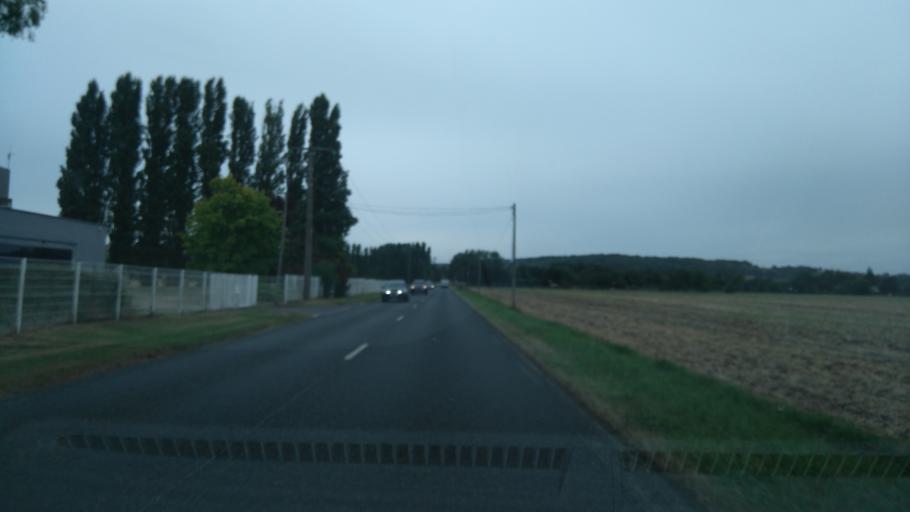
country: FR
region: Picardie
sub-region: Departement de l'Oise
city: Precy-sur-Oise
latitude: 49.1972
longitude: 2.3797
